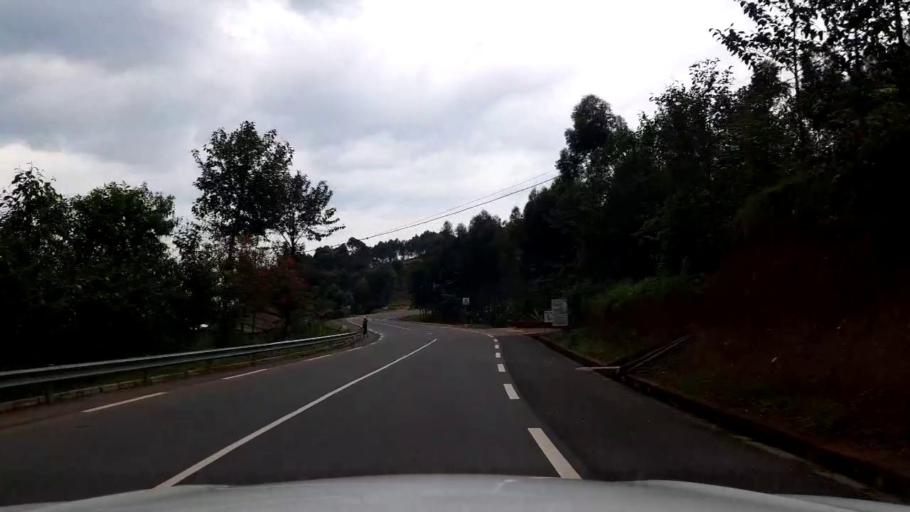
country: RW
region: Western Province
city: Kibuye
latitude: -1.8880
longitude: 29.3460
